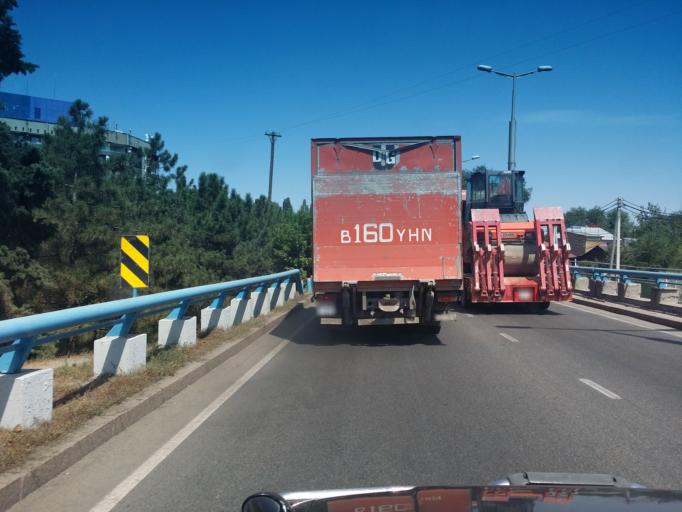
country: KZ
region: Almaty Oblysy
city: Pervomayskiy
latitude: 43.3407
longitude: 76.9846
